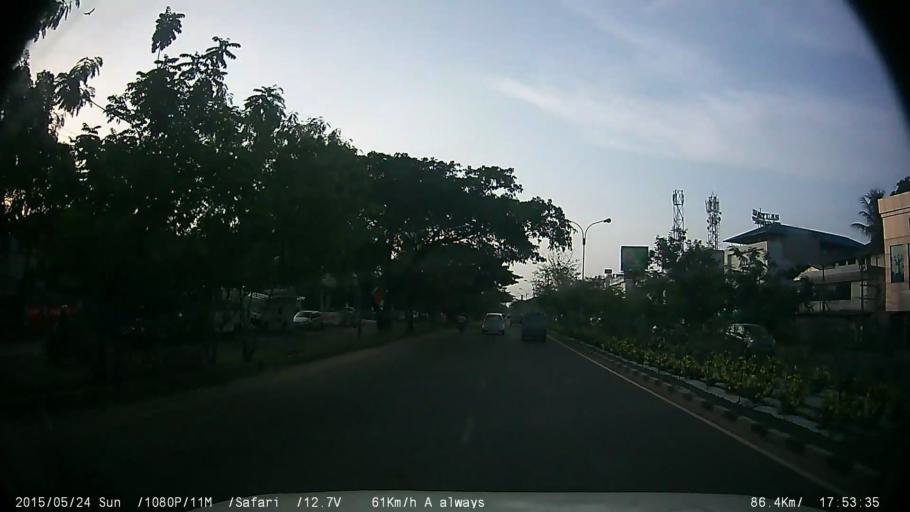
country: IN
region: Kerala
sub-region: Ernakulam
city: Elur
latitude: 10.0090
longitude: 76.3123
